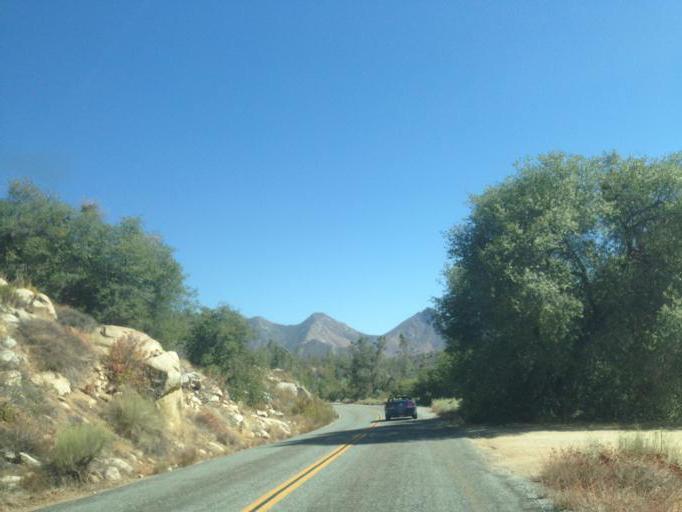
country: US
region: California
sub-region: Kern County
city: Kernville
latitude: 35.8950
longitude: -118.4660
